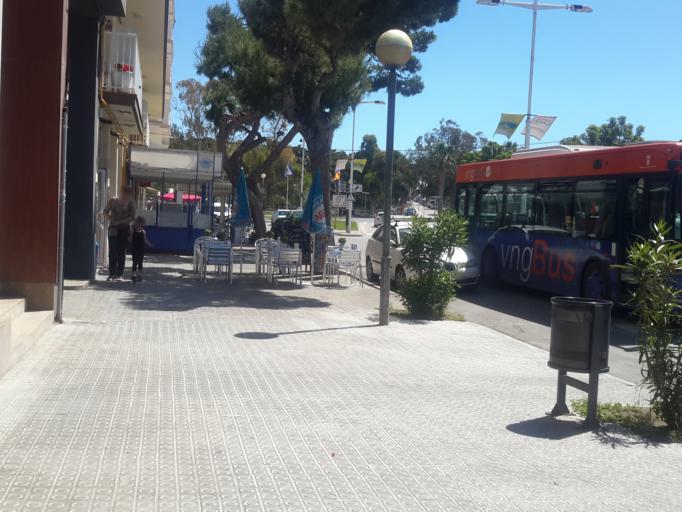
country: ES
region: Catalonia
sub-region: Provincia de Barcelona
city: Vilanova i la Geltru
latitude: 41.2169
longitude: 1.7341
